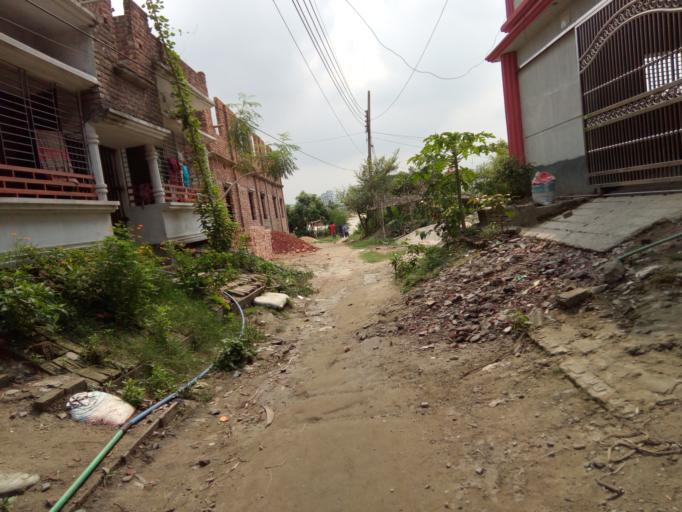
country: BD
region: Dhaka
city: Paltan
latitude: 23.7591
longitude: 90.4523
